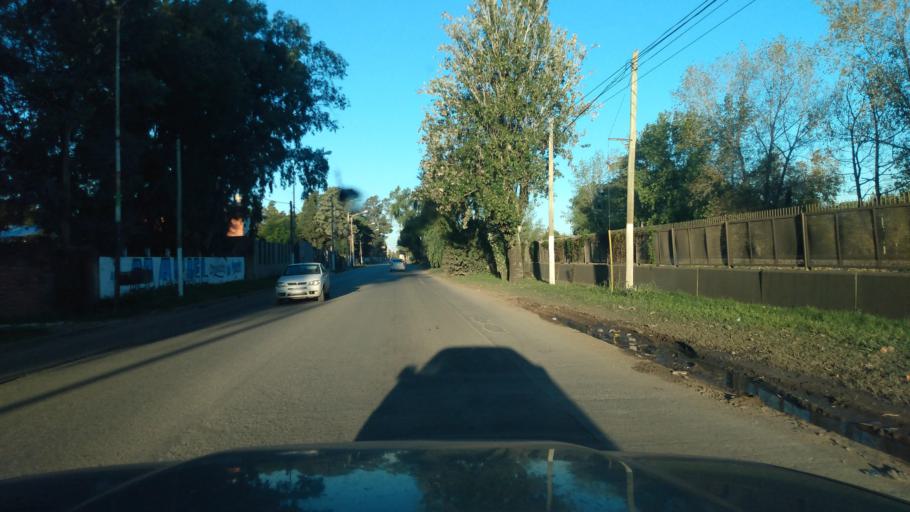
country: AR
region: Buenos Aires
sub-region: Partido de Merlo
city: Merlo
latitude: -34.6452
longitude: -58.8081
